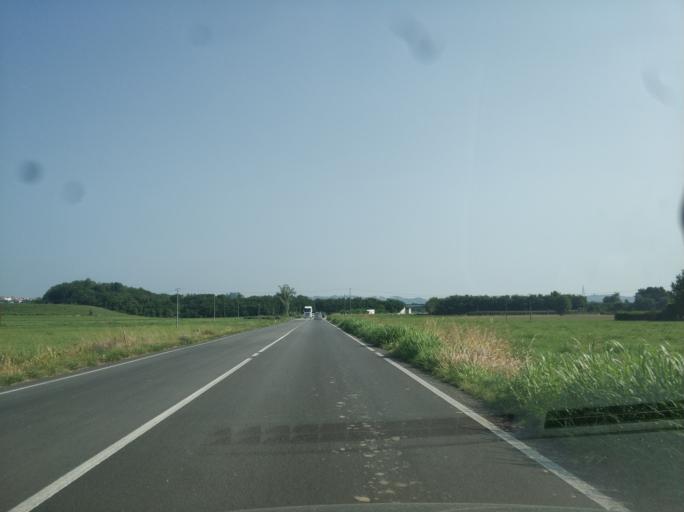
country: IT
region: Piedmont
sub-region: Provincia di Cuneo
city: Roreto
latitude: 44.6706
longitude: 7.8614
